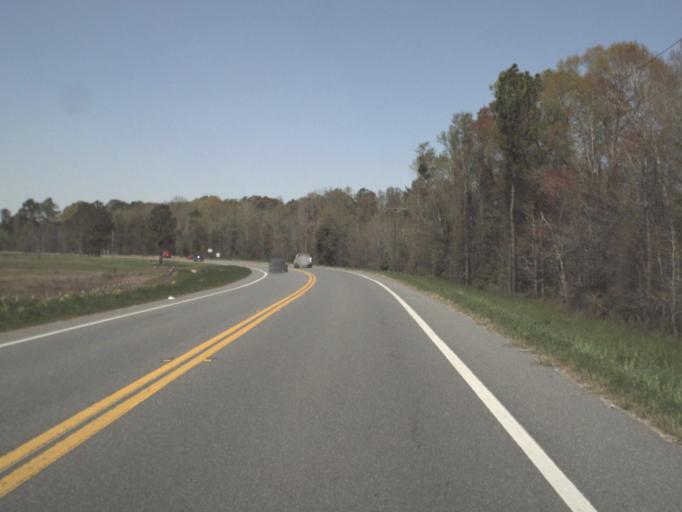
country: US
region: Florida
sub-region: Jackson County
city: Graceville
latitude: 30.9707
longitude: -85.6112
